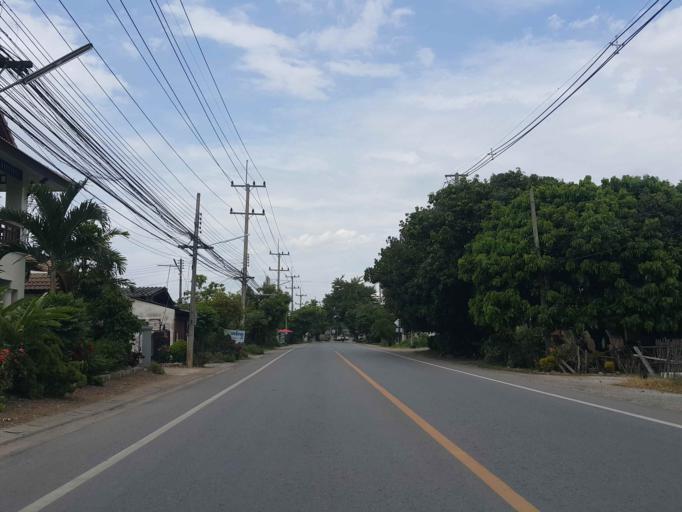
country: TH
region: Lamphun
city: Lamphun
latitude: 18.6233
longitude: 99.0351
